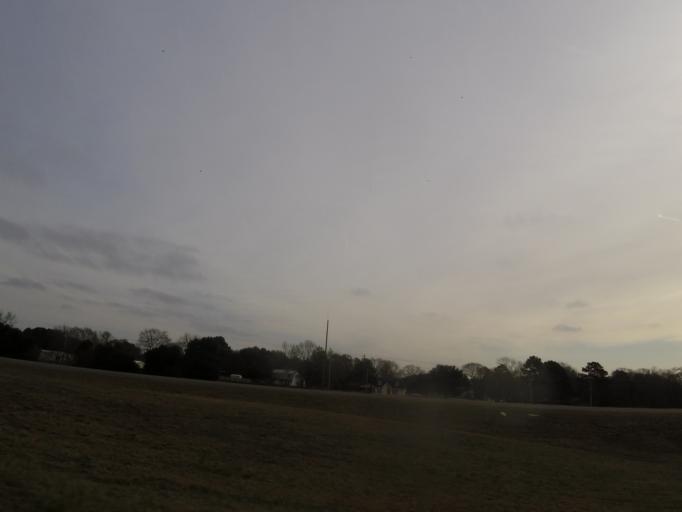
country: US
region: Alabama
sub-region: Autauga County
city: Pine Level
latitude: 32.5679
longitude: -86.4657
